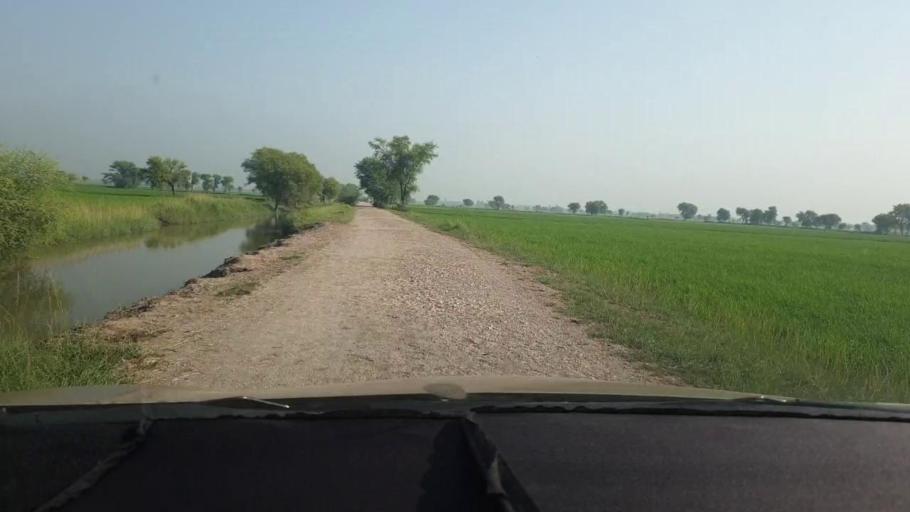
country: PK
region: Sindh
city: Kambar
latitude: 27.5842
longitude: 68.1021
